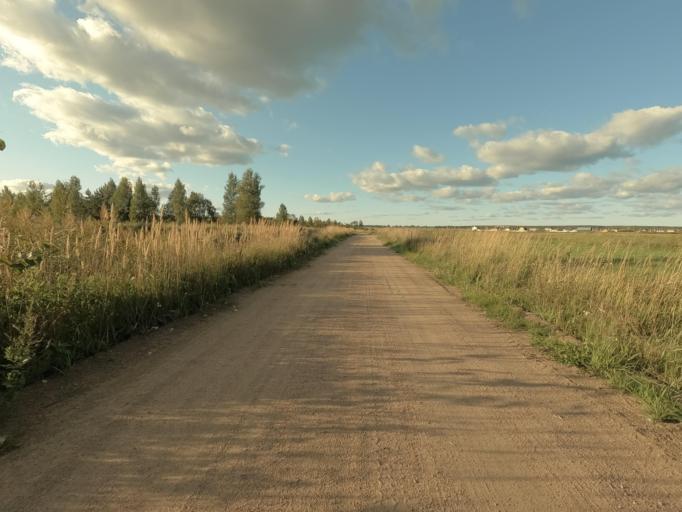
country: RU
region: Leningrad
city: Imeni Sverdlova
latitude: 59.8625
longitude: 30.7306
